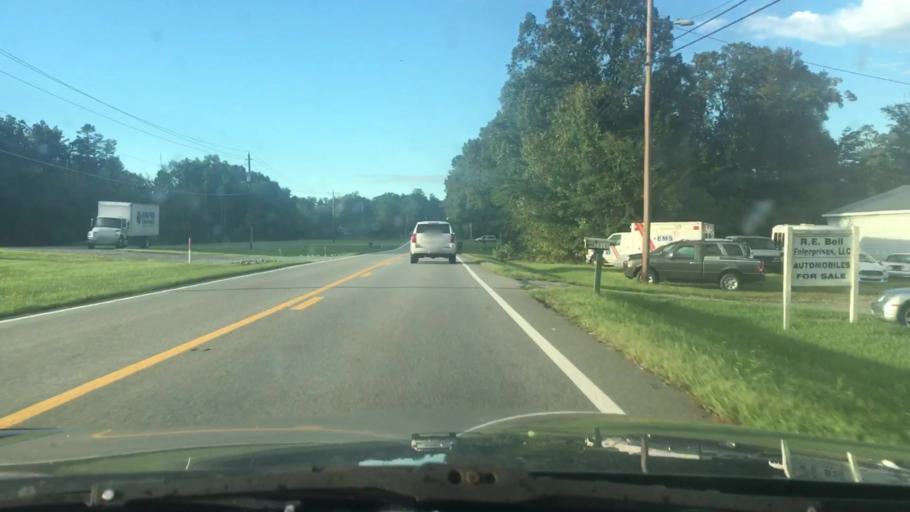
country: US
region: North Carolina
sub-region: Alamance County
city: Green Level
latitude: 36.1502
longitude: -79.3382
